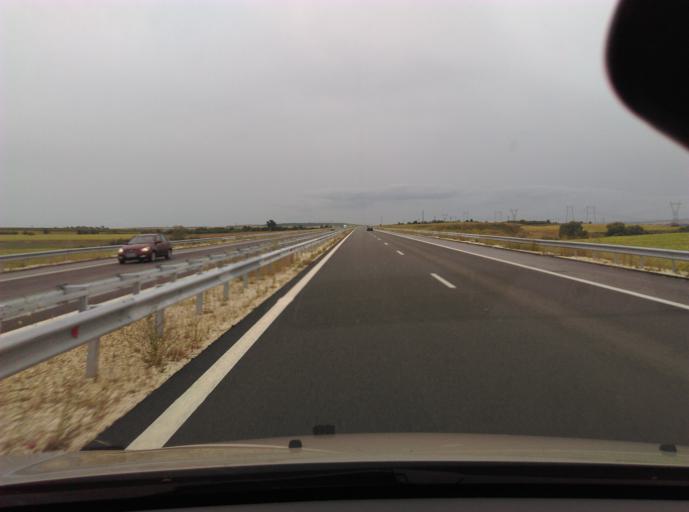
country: BG
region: Stara Zagora
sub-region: Obshtina Chirpan
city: Chirpan
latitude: 42.1357
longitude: 25.3427
